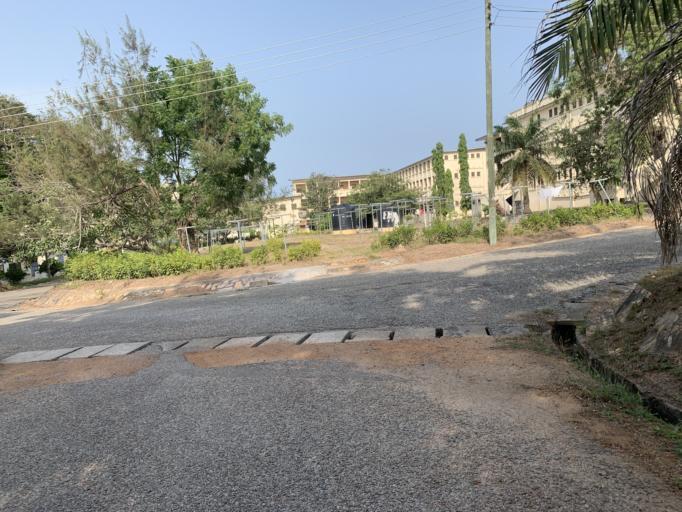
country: GH
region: Central
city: Winneba
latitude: 5.3379
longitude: -0.6265
